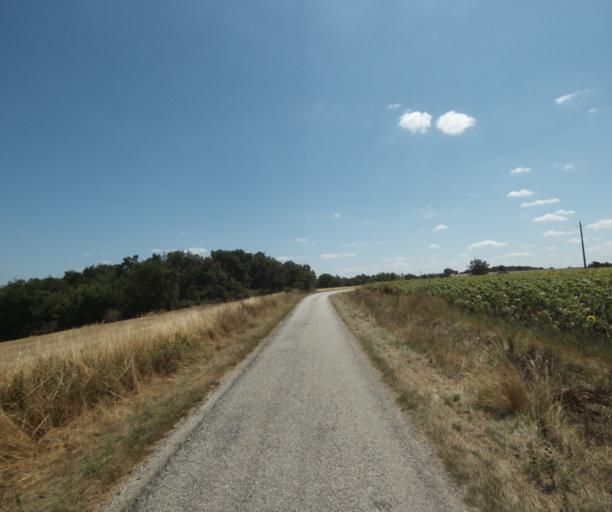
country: FR
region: Midi-Pyrenees
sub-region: Departement de la Haute-Garonne
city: Auriac-sur-Vendinelle
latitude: 43.4944
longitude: 1.8554
